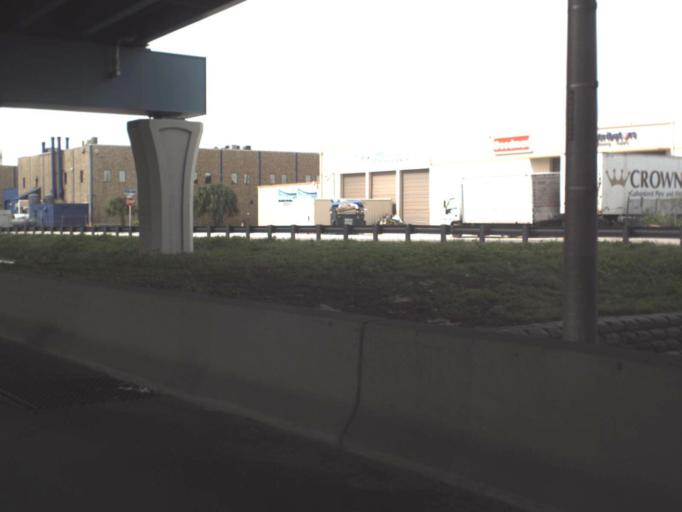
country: US
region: Florida
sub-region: Miami-Dade County
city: Virginia Gardens
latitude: 25.7972
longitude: -80.3175
